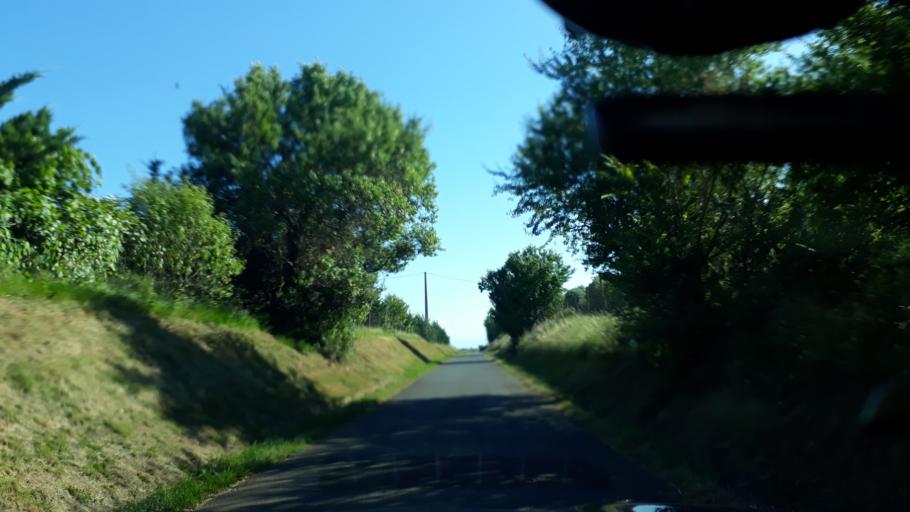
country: FR
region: Languedoc-Roussillon
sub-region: Departement de l'Herault
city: Marseillan
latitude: 43.3329
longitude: 3.5029
